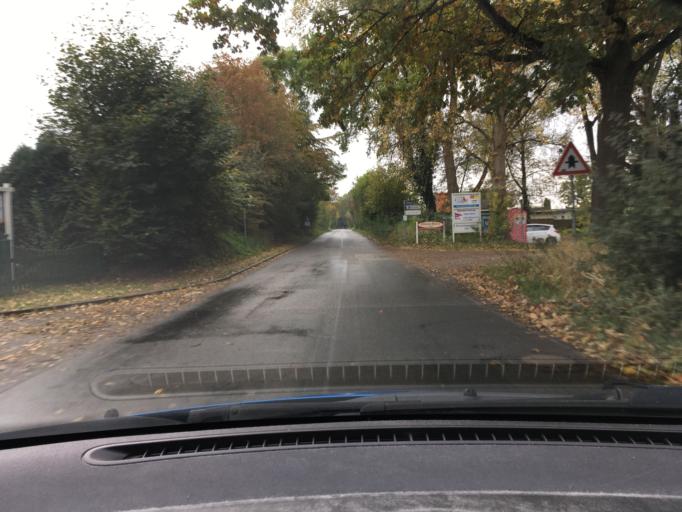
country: DE
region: Schleswig-Holstein
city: Bosau
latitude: 54.1021
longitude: 10.4300
